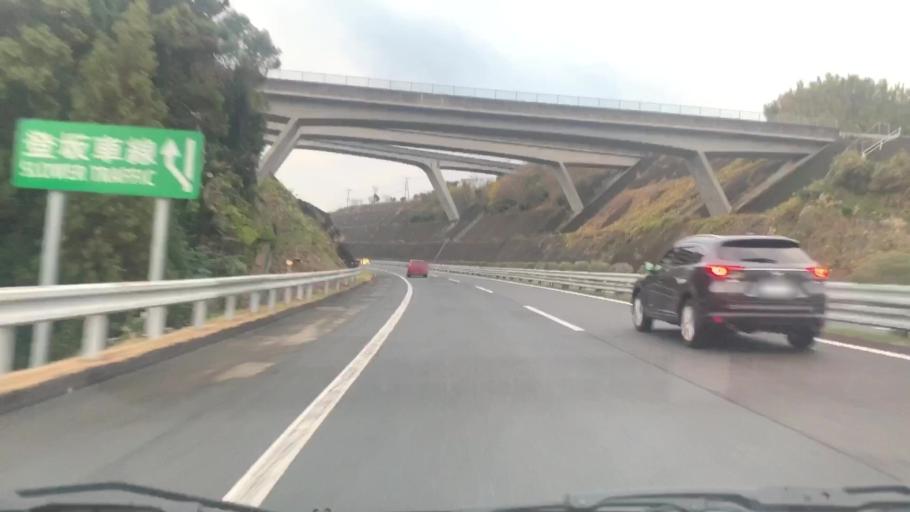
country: JP
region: Nagasaki
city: Omura
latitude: 33.0001
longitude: 129.9511
